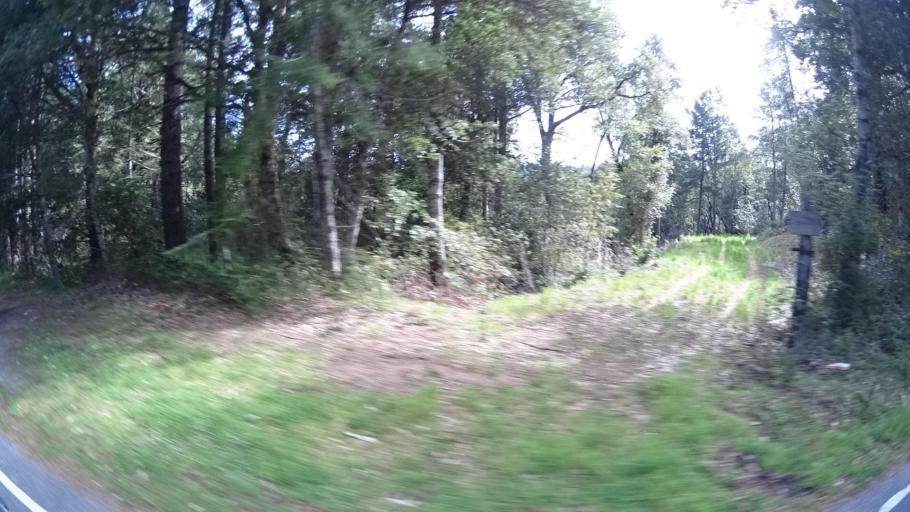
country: US
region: California
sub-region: Humboldt County
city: Blue Lake
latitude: 40.7448
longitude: -123.9637
